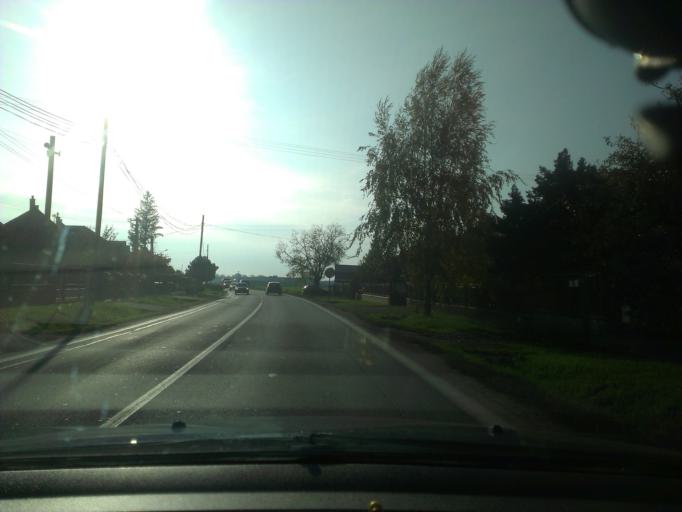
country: SK
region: Nitriansky
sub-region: Okres Nitra
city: Nitra
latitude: 48.3487
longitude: 18.0603
